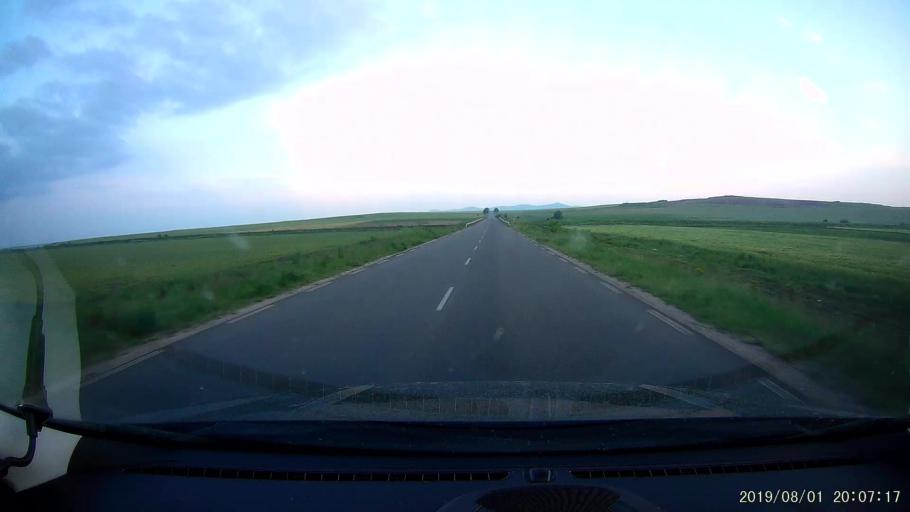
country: BG
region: Yambol
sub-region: Obshtina Yambol
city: Yambol
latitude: 42.5247
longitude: 26.5663
